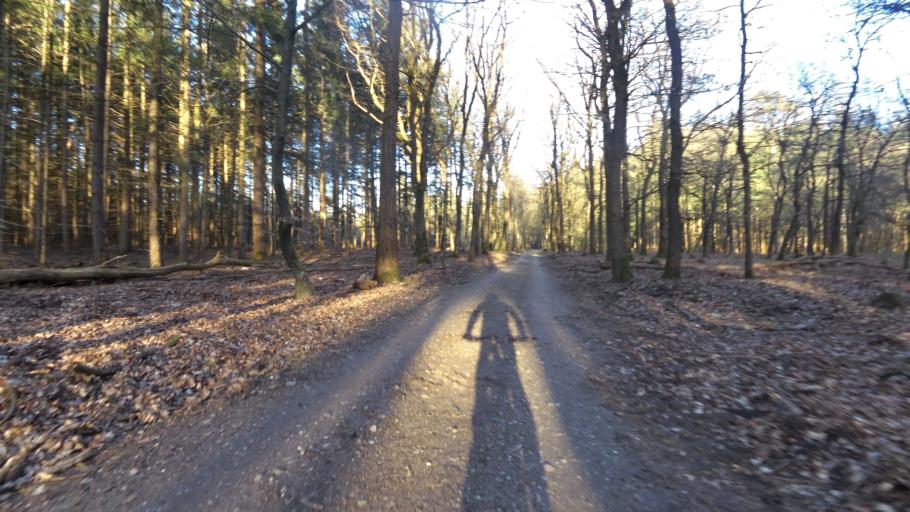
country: NL
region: Gelderland
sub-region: Gemeente Putten
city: Putten
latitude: 52.2569
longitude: 5.6418
